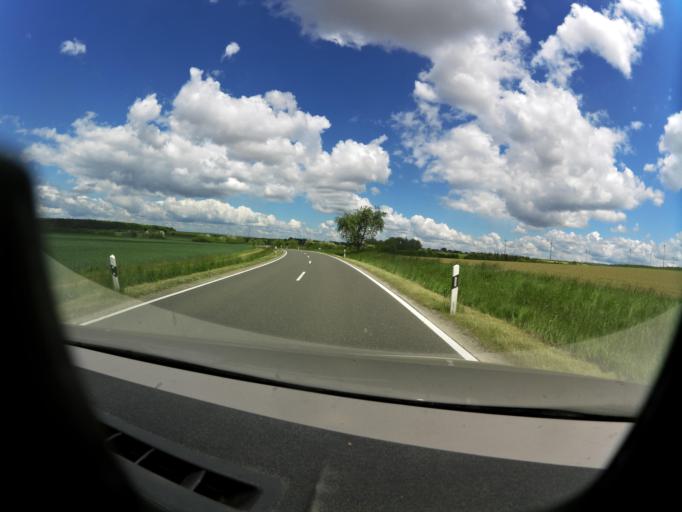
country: DE
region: Bavaria
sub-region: Regierungsbezirk Unterfranken
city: Prosselsheim
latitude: 49.8887
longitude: 10.1212
